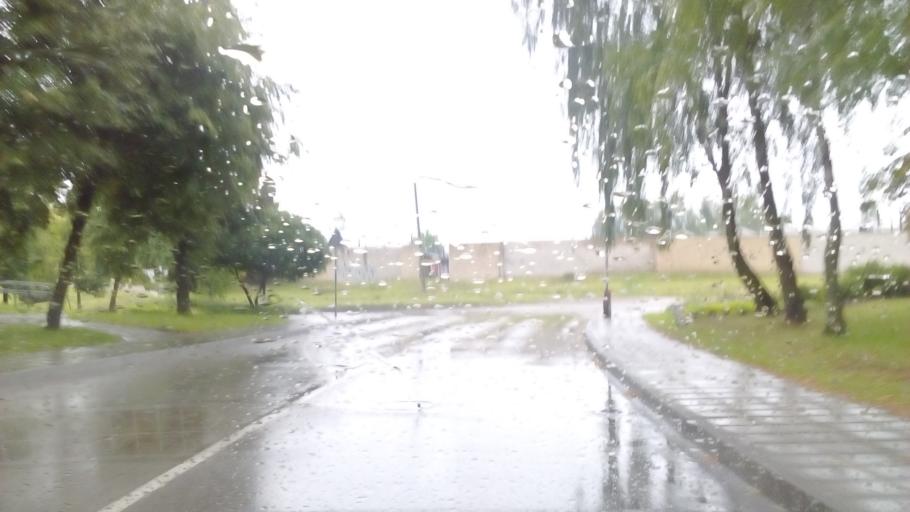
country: LT
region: Alytaus apskritis
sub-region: Alytus
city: Alytus
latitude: 54.3933
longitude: 24.0326
